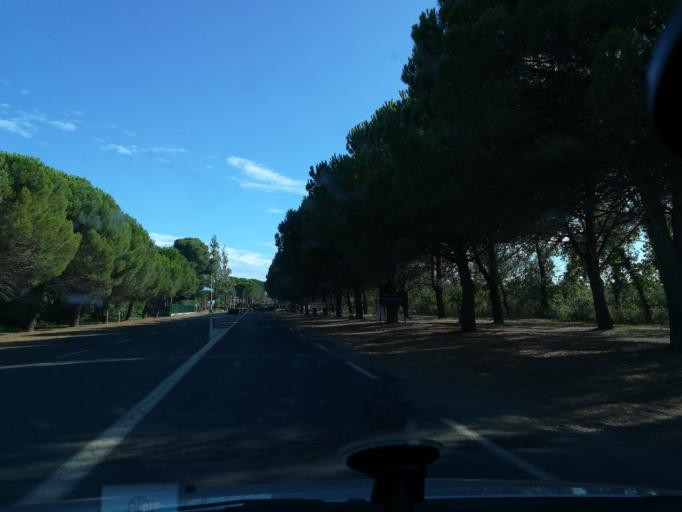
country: FR
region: Languedoc-Roussillon
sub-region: Departement de l'Herault
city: Portiragnes
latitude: 43.2856
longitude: 3.3626
